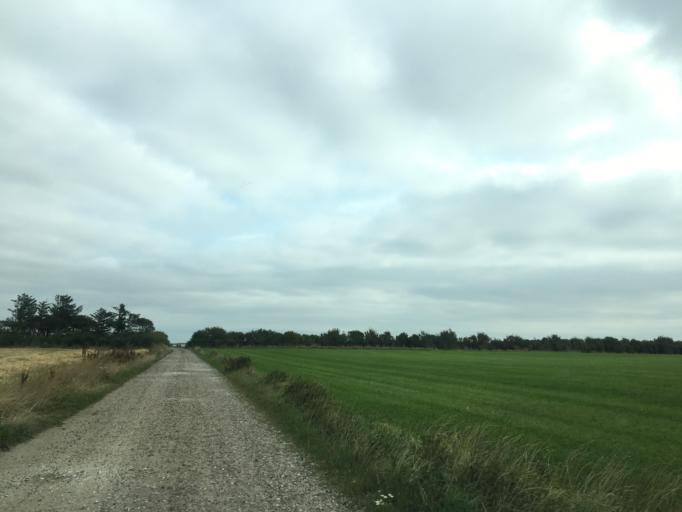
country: DK
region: Central Jutland
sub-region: Lemvig Kommune
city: Thyboron
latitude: 56.7884
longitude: 8.2772
